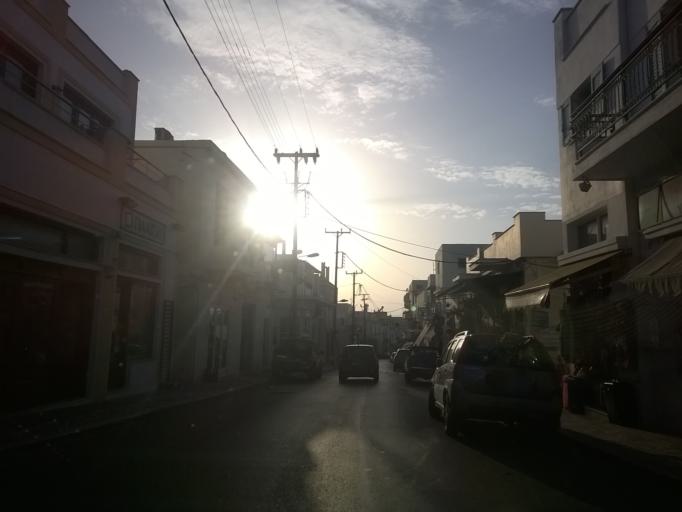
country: GR
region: South Aegean
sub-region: Nomos Kykladon
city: Naxos
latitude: 37.1032
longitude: 25.3772
